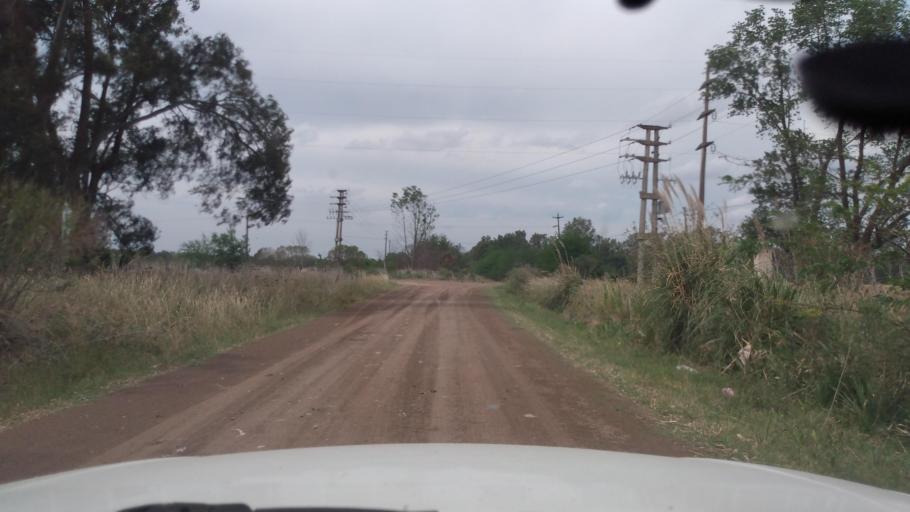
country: AR
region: Buenos Aires
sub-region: Partido de Lujan
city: Lujan
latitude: -34.5513
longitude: -59.1699
